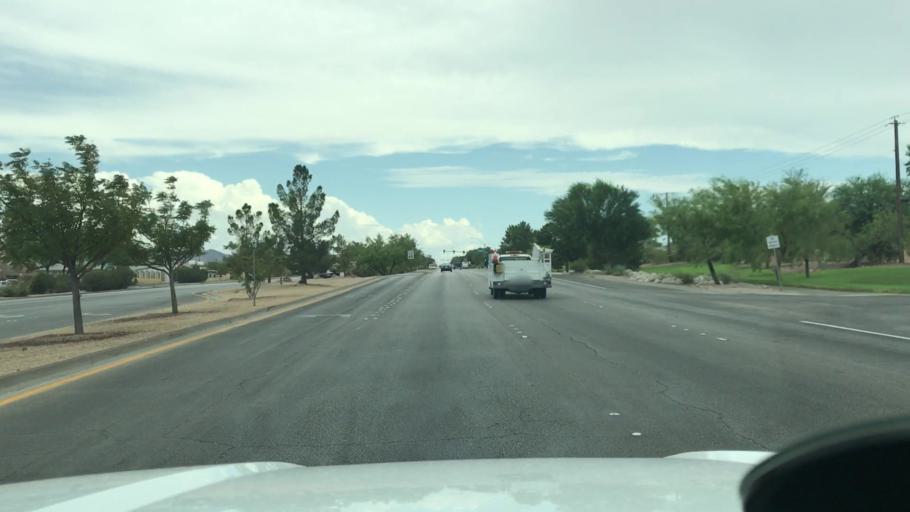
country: US
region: Nevada
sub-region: Clark County
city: Henderson
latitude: 36.0387
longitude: -114.9812
